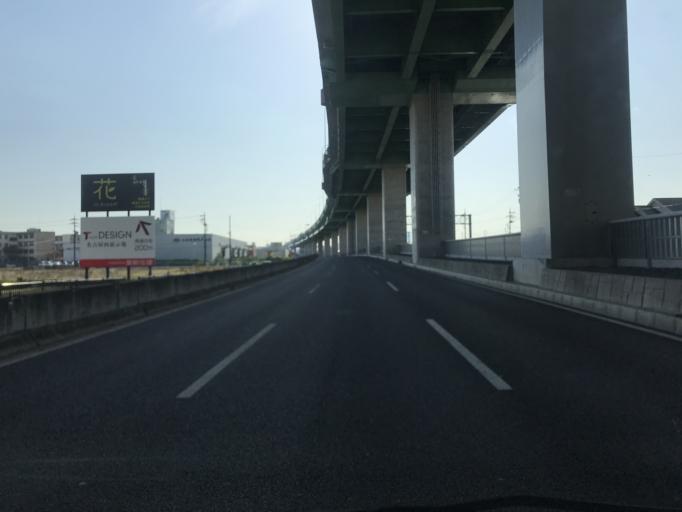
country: JP
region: Aichi
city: Nagoya-shi
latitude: 35.2162
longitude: 136.8578
